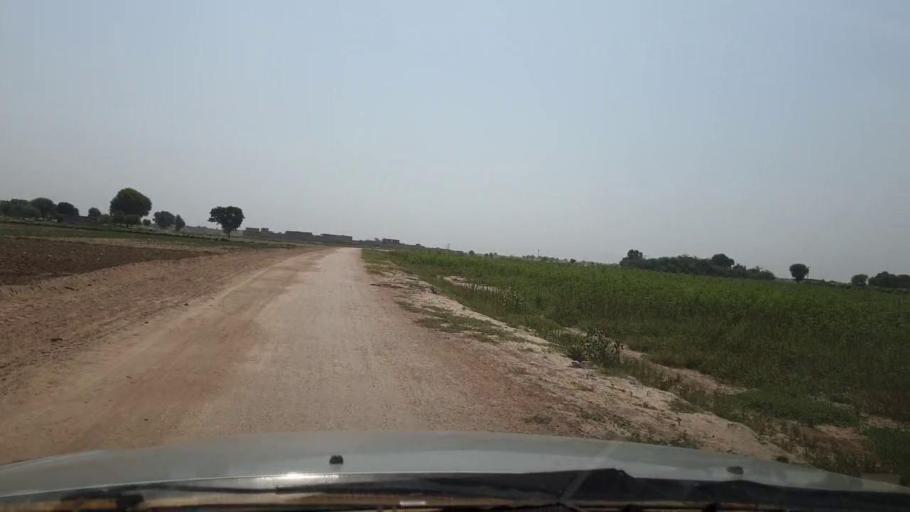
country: PK
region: Sindh
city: Chambar
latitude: 25.2637
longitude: 68.7576
